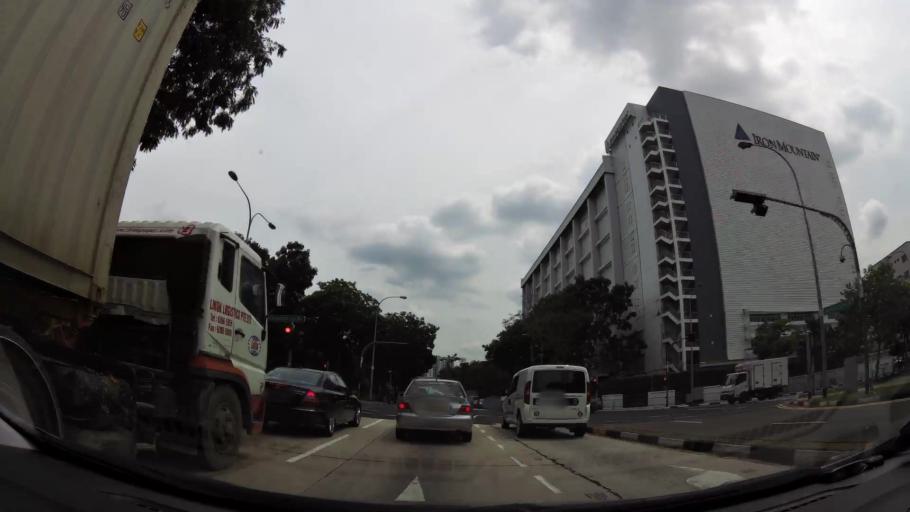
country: MY
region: Johor
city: Johor Bahru
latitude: 1.3376
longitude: 103.7174
